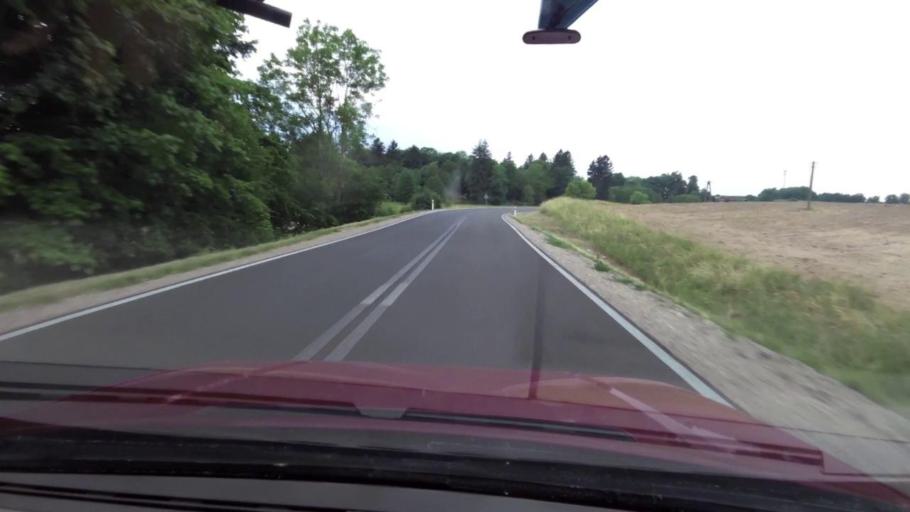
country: PL
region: West Pomeranian Voivodeship
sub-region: Powiat koszalinski
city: Sianow
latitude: 54.1584
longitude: 16.4539
